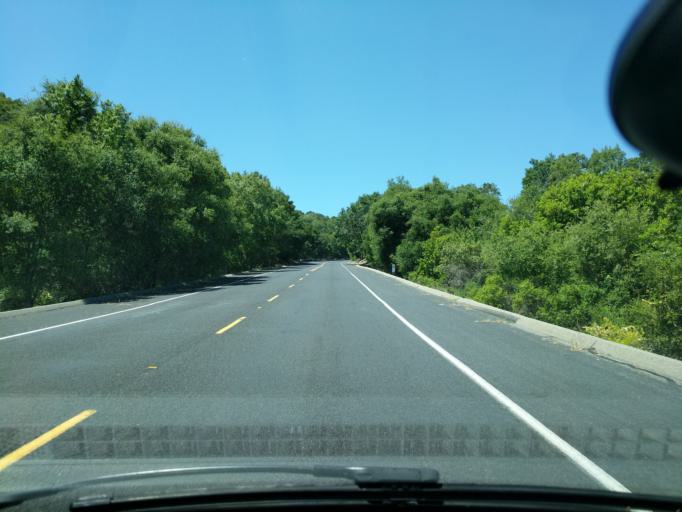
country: US
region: California
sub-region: Contra Costa County
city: Orinda
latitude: 37.9188
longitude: -122.1695
